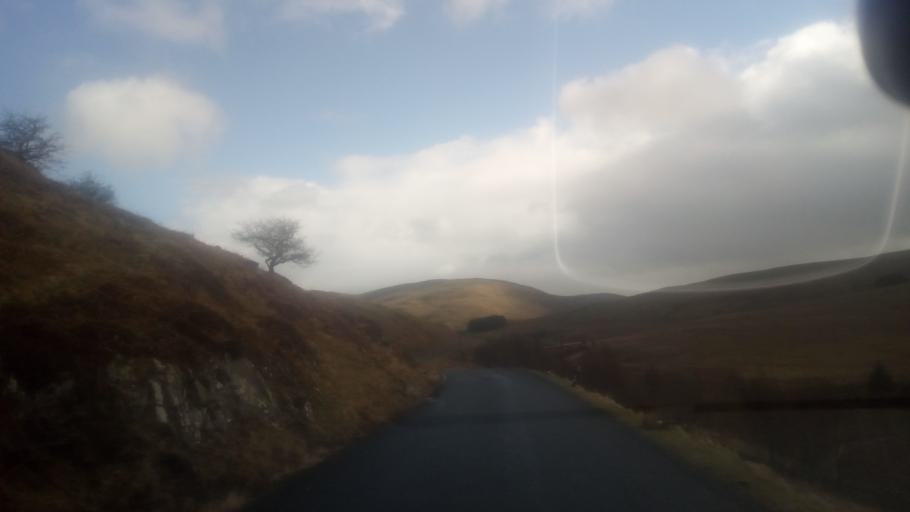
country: GB
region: Scotland
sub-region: The Scottish Borders
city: Innerleithen
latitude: 55.4626
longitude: -3.1227
